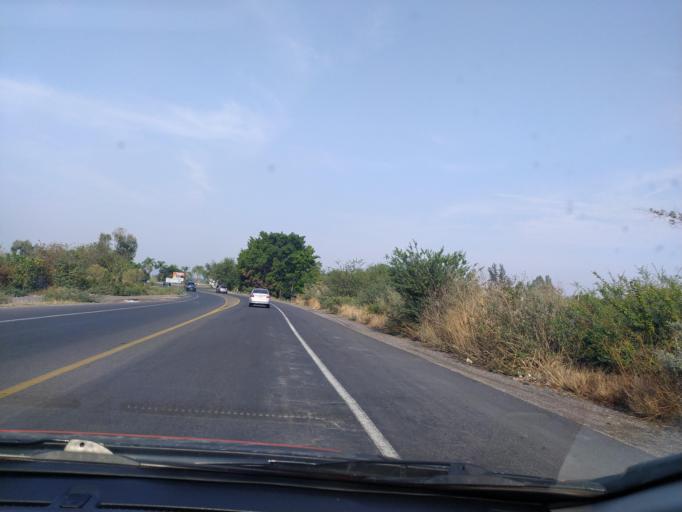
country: MX
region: Jalisco
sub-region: Acatlan de Juarez
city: Villa de los Ninos
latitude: 20.4137
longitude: -103.5914
